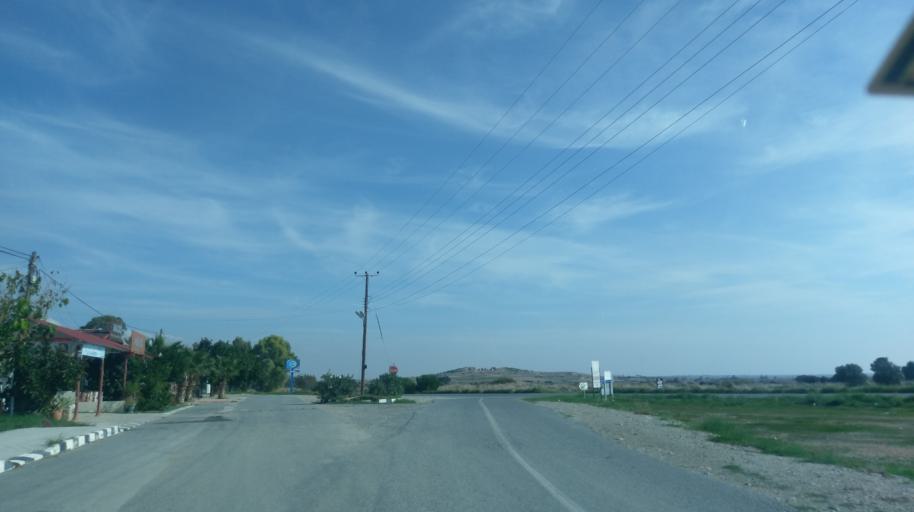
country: CY
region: Ammochostos
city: Lefkonoiko
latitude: 35.2475
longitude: 33.6106
